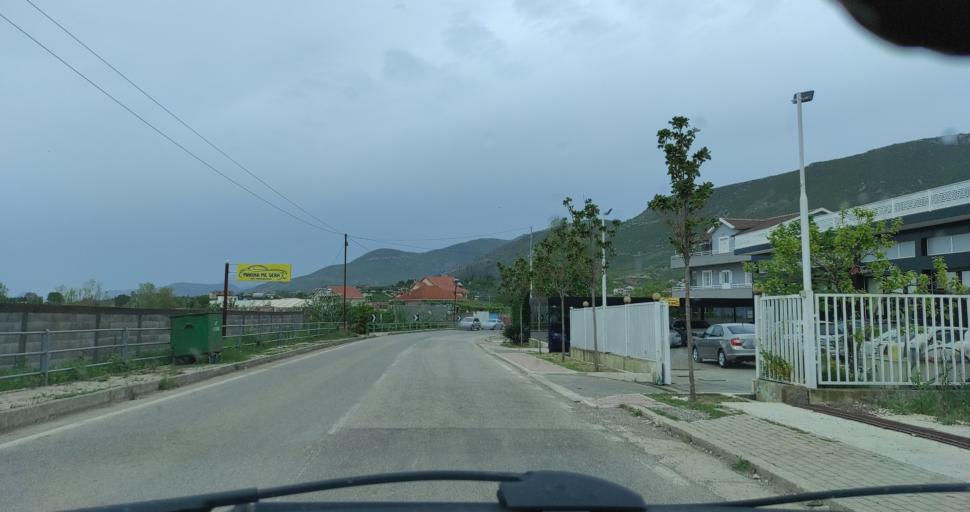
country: AL
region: Lezhe
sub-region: Rrethi i Kurbinit
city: Lac
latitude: 41.6076
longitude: 19.7124
